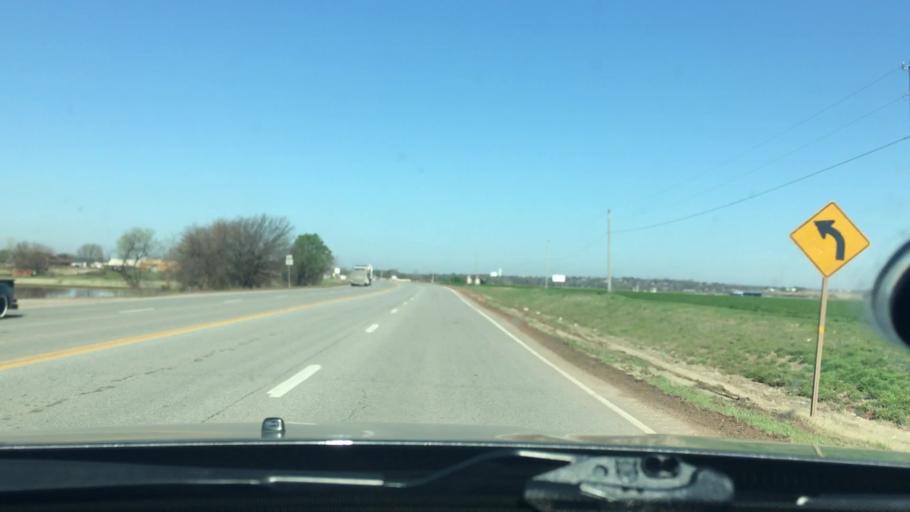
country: US
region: Oklahoma
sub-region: Garvin County
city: Lindsay
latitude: 34.8342
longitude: -97.5826
